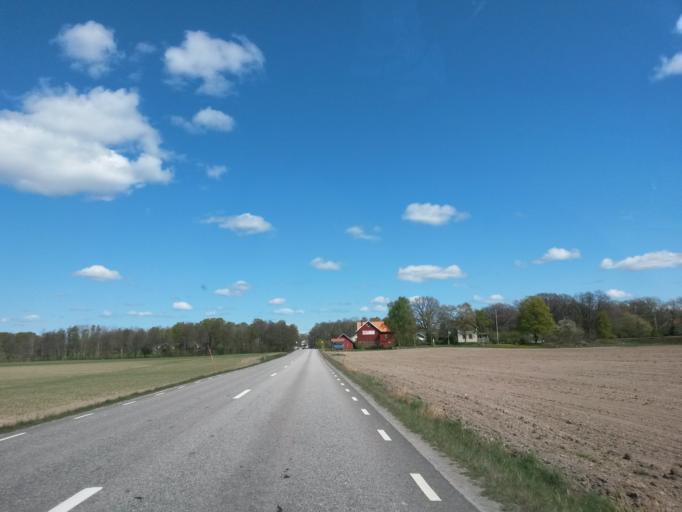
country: SE
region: Vaestra Goetaland
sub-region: Herrljunga Kommun
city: Herrljunga
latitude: 58.0732
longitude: 12.9953
